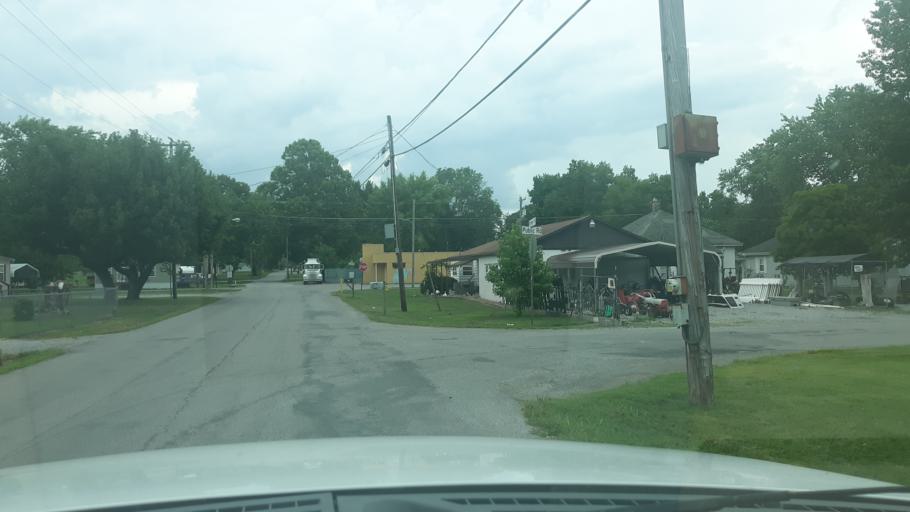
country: US
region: Illinois
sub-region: Saline County
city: Eldorado
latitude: 37.8066
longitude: -88.4566
